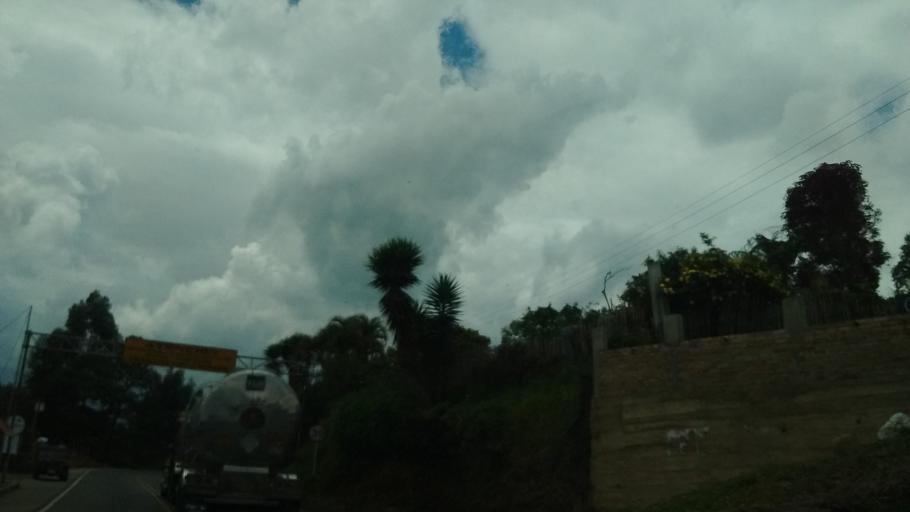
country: CO
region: Cauca
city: Rosas
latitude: 2.3129
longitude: -76.6850
